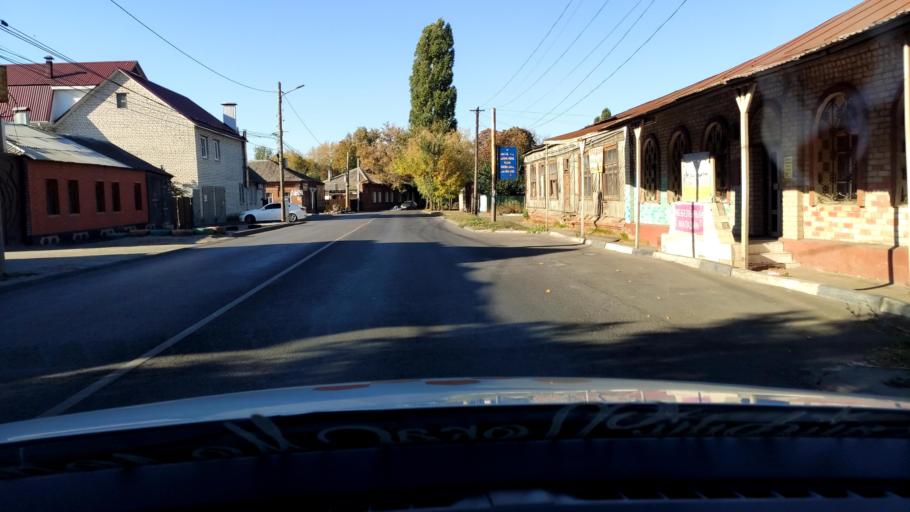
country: RU
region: Voronezj
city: Voronezh
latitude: 51.6824
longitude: 39.2111
